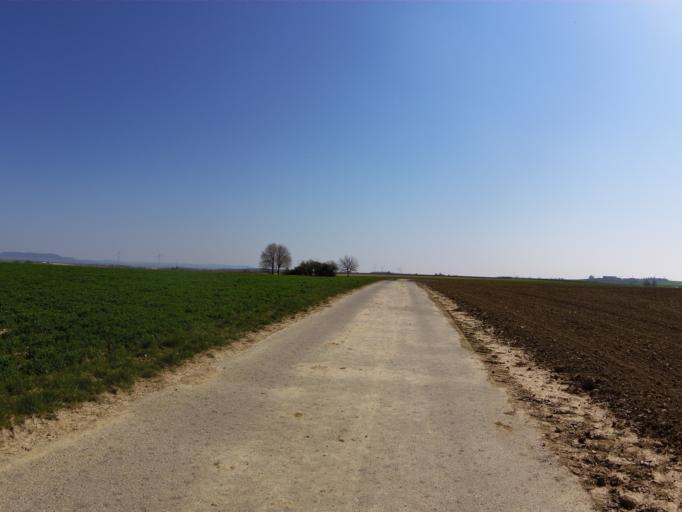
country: DE
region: Bavaria
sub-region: Regierungsbezirk Unterfranken
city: Biebelried
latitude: 49.8096
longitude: 10.0793
